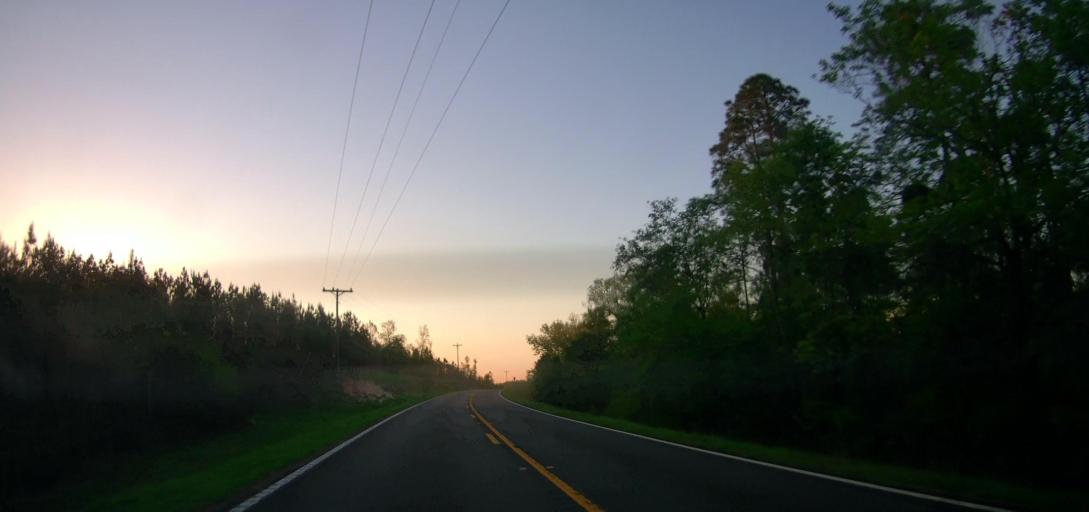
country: US
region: Georgia
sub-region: Marion County
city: Buena Vista
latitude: 32.3947
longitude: -84.5730
